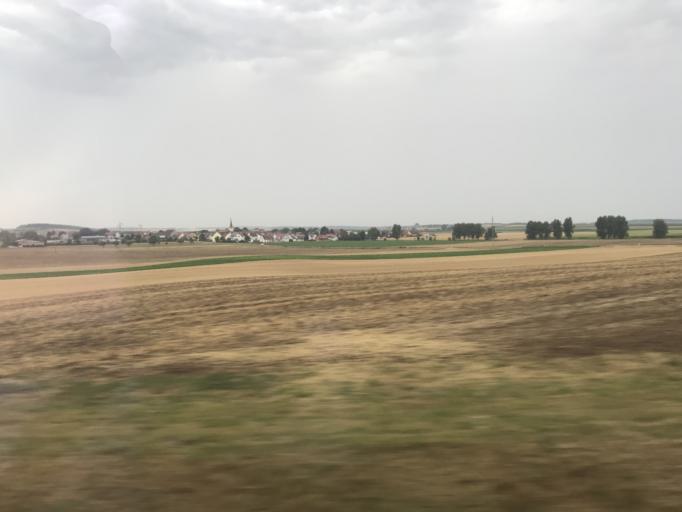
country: DE
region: Bavaria
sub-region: Regierungsbezirk Unterfranken
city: Bergtheim
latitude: 49.9217
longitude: 10.0904
